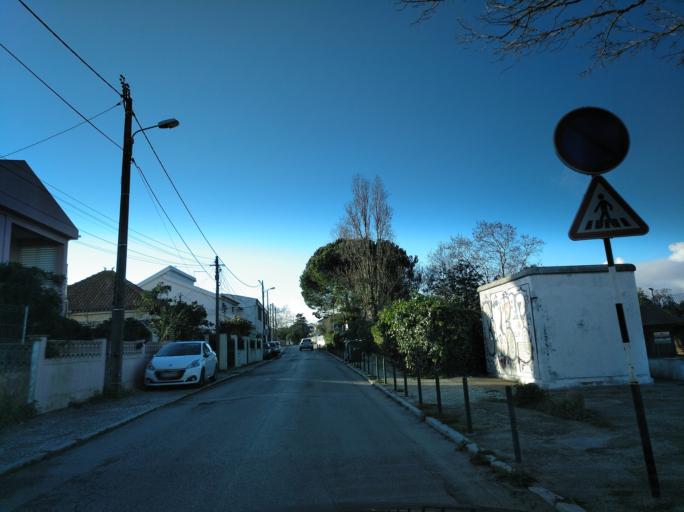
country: PT
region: Setubal
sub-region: Almada
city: Sobreda
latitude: 38.6470
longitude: -9.1927
